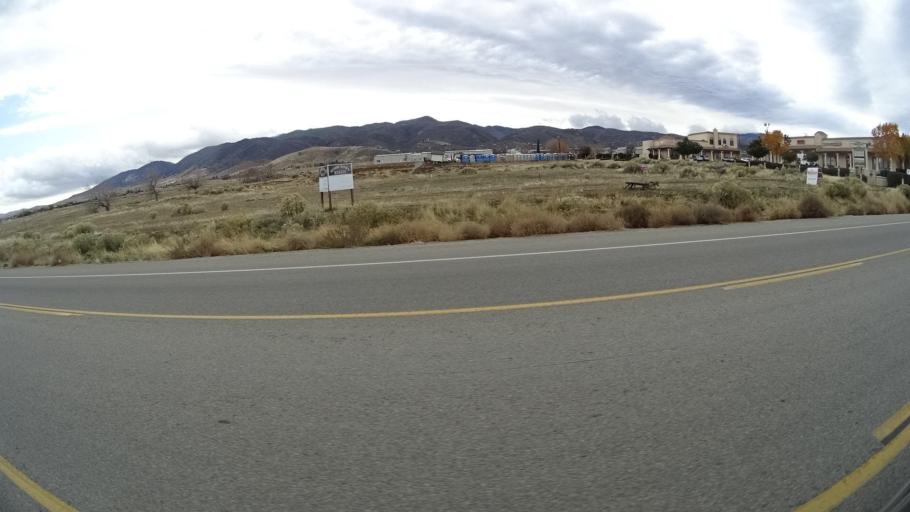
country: US
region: California
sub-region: Kern County
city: Golden Hills
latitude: 35.1244
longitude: -118.4896
